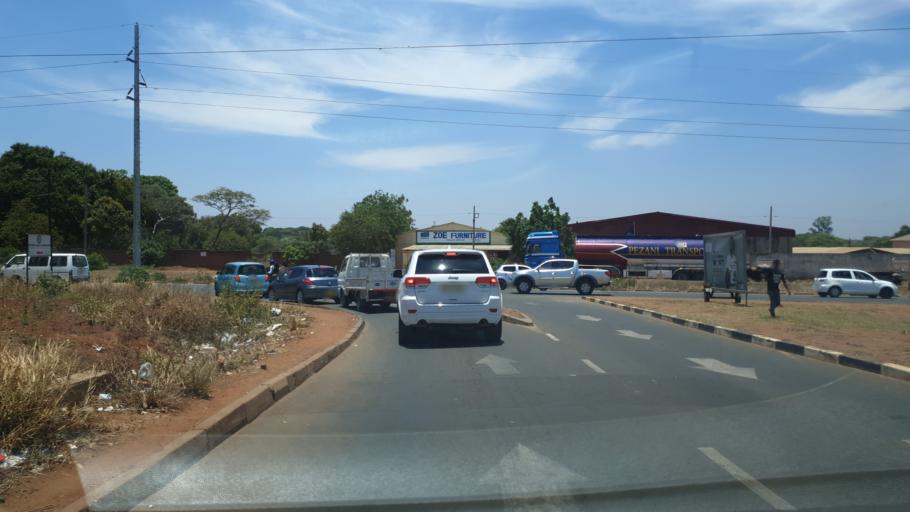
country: MW
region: Central Region
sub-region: Lilongwe District
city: Lilongwe
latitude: -13.9722
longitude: 33.7401
